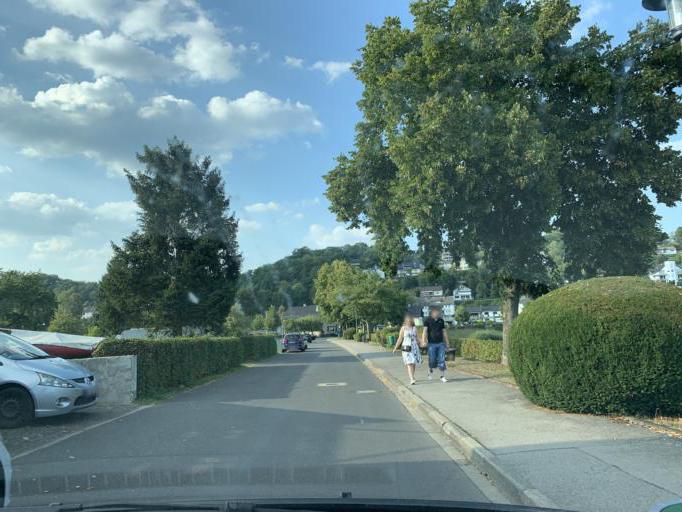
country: DE
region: North Rhine-Westphalia
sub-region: Regierungsbezirk Koln
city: Simmerath
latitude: 50.6099
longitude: 6.3848
